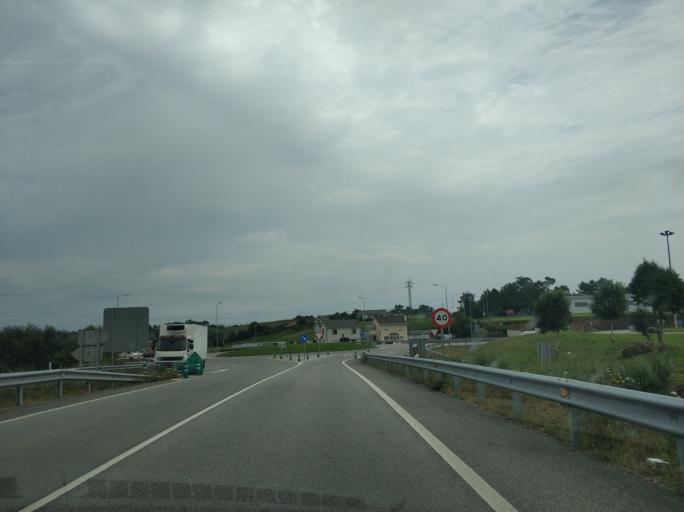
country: ES
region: Asturias
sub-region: Province of Asturias
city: Navia
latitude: 43.5280
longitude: -6.5521
